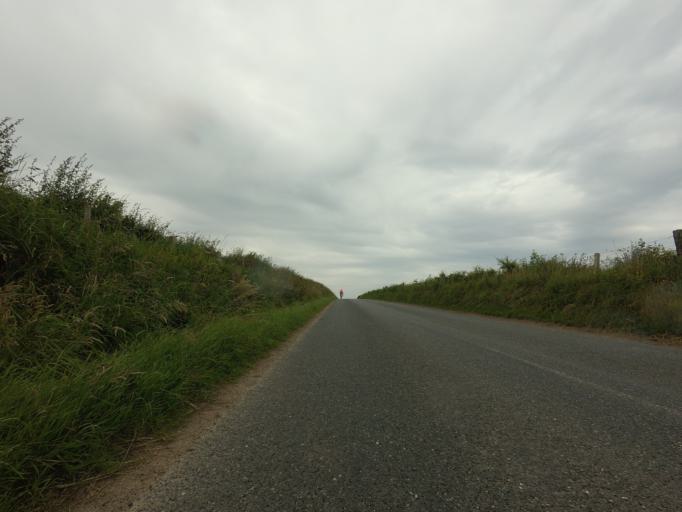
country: GB
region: Scotland
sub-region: Aberdeenshire
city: Whitehills
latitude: 57.6706
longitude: -2.6152
